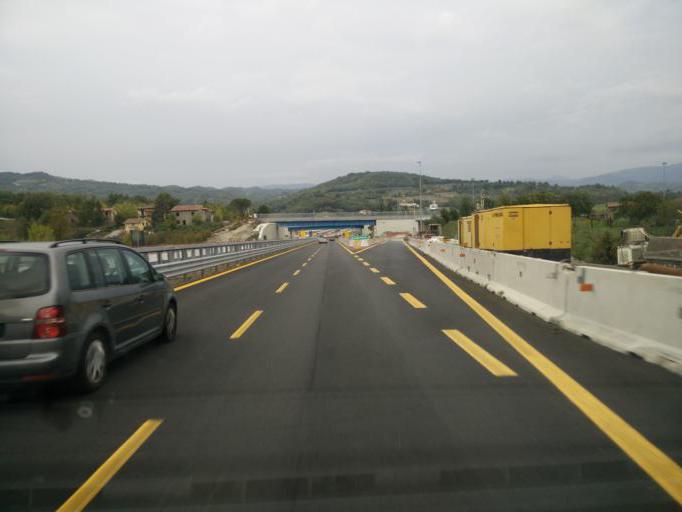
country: IT
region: Tuscany
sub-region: Province of Florence
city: Cavallina
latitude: 43.9805
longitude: 11.2113
